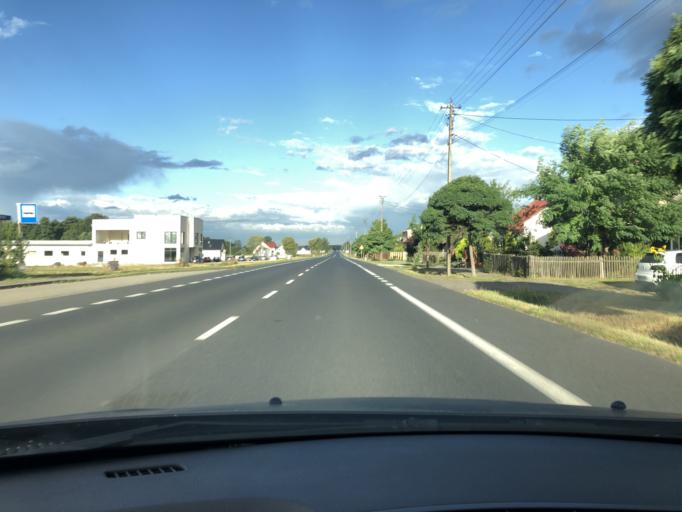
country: PL
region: Lodz Voivodeship
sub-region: Powiat wieruszowski
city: Galewice
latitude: 51.3036
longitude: 18.2711
